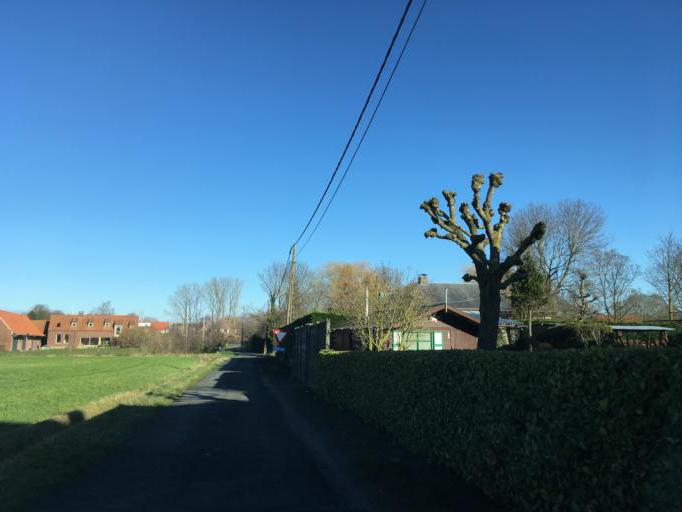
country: BE
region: Flanders
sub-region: Provincie West-Vlaanderen
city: Roeselare
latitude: 50.9229
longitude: 3.1278
